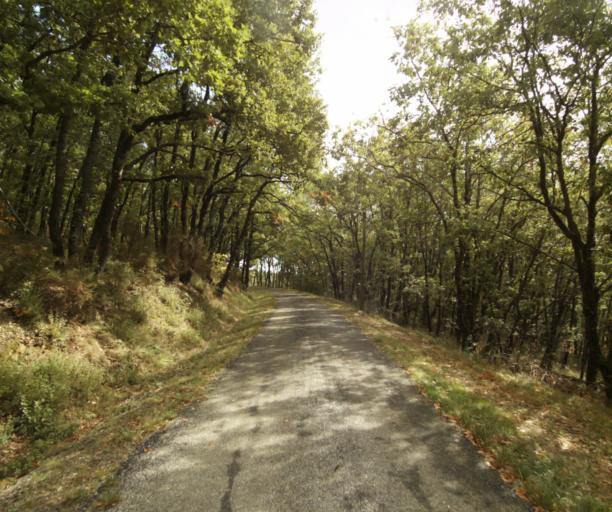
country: FR
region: Midi-Pyrenees
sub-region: Departement du Tarn-et-Garonne
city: Beaumont-de-Lomagne
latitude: 43.8626
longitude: 1.0858
